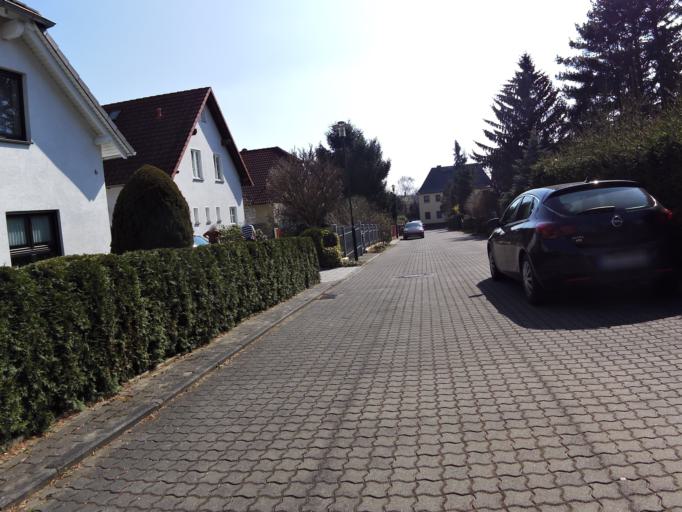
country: DE
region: Saxony
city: Leipzig
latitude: 51.3803
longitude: 12.3028
